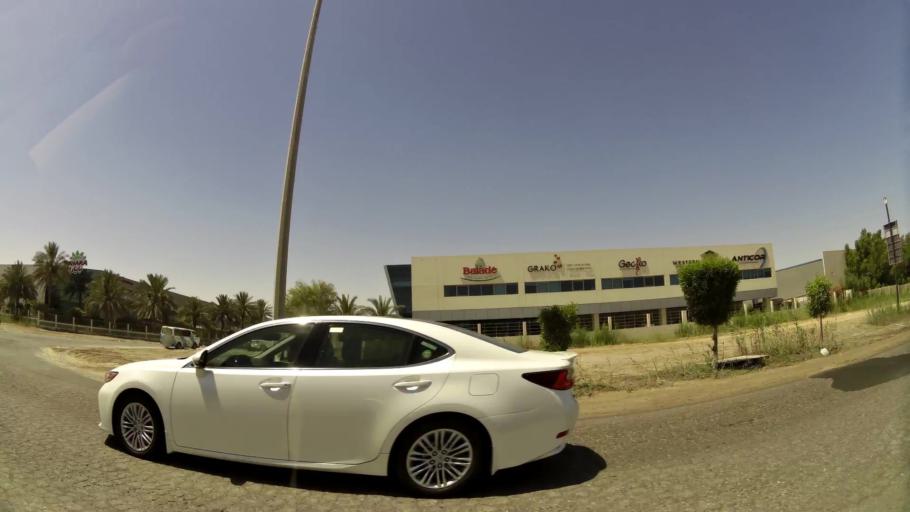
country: AE
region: Dubai
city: Dubai
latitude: 24.9849
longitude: 55.1943
